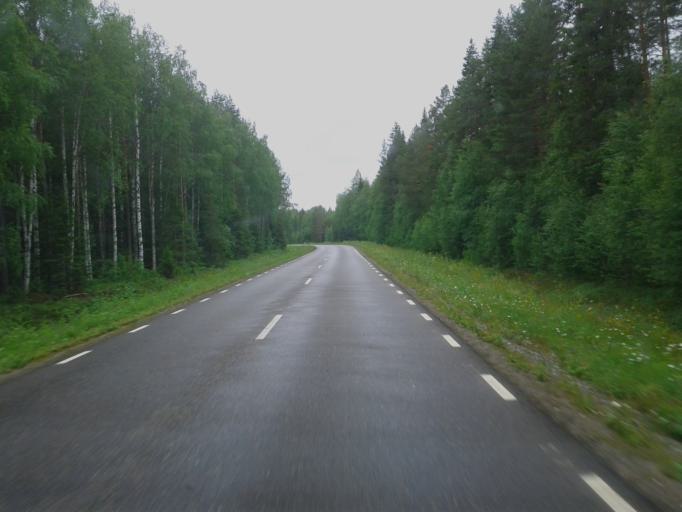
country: SE
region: Vaesterbotten
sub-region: Skelleftea Kommun
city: Kage
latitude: 64.9195
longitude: 20.8785
